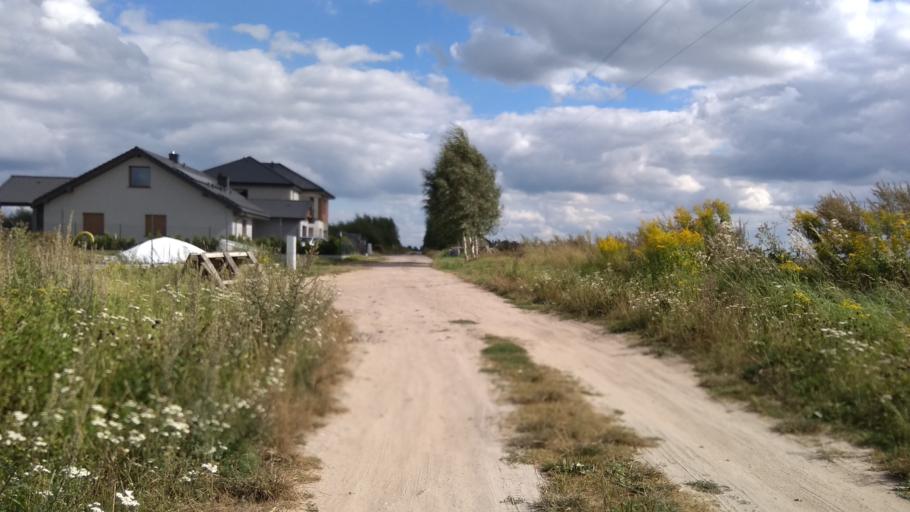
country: PL
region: Kujawsko-Pomorskie
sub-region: Powiat bydgoski
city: Osielsko
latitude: 53.2211
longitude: 18.1429
